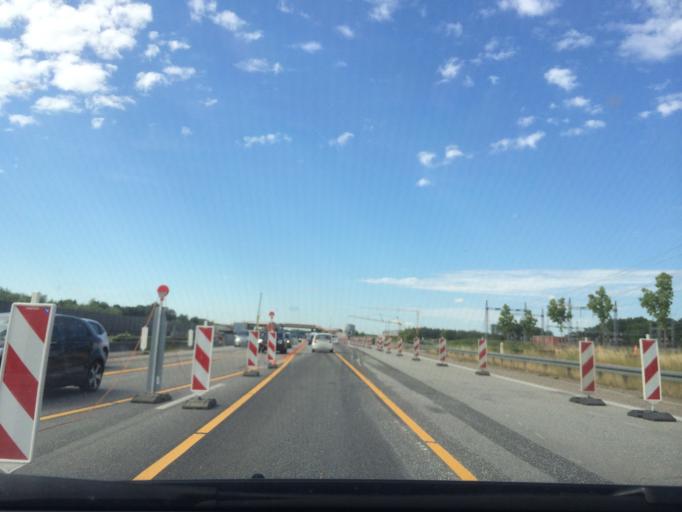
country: DK
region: Zealand
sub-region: Greve Kommune
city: Greve
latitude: 55.5854
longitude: 12.2630
